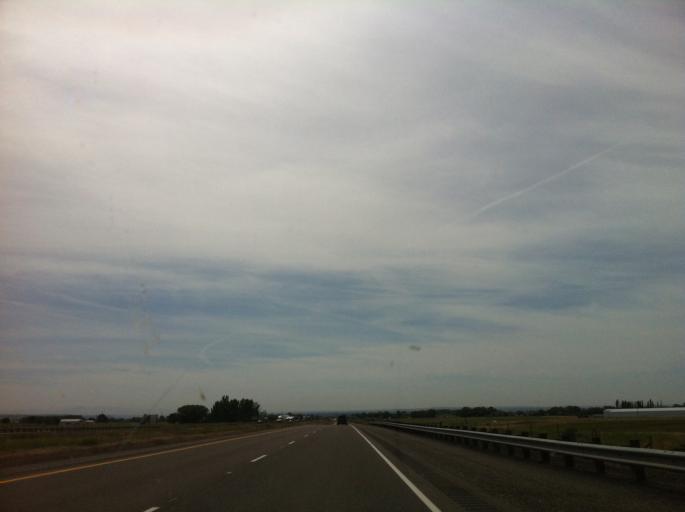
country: US
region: Oregon
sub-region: Malheur County
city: Ontario
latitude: 44.0936
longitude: -117.0314
